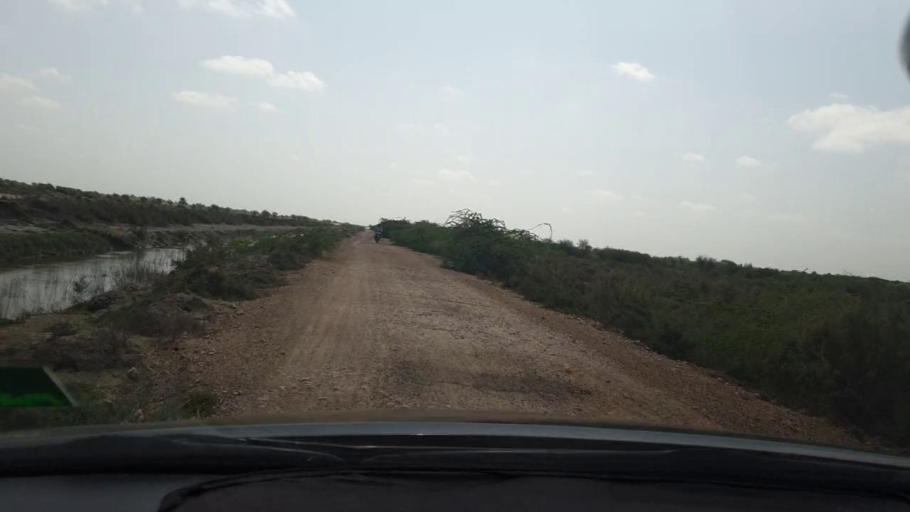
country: PK
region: Sindh
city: Tando Bago
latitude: 24.8294
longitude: 69.0604
